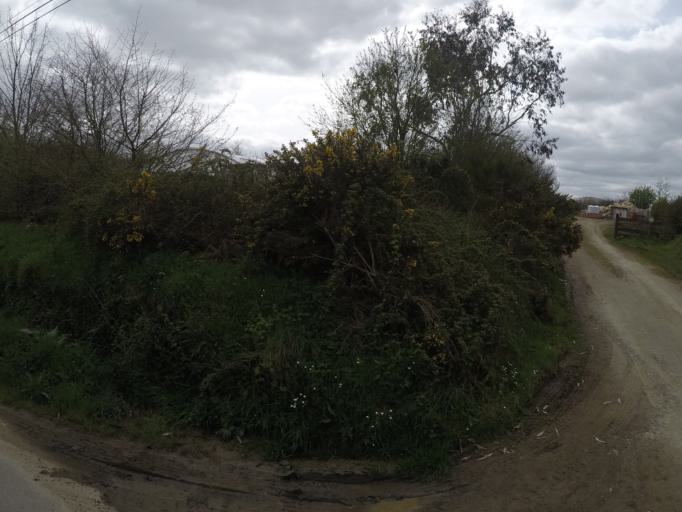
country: FR
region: Brittany
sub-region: Departement des Cotes-d'Armor
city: Plouha
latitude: 48.7065
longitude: -2.9369
